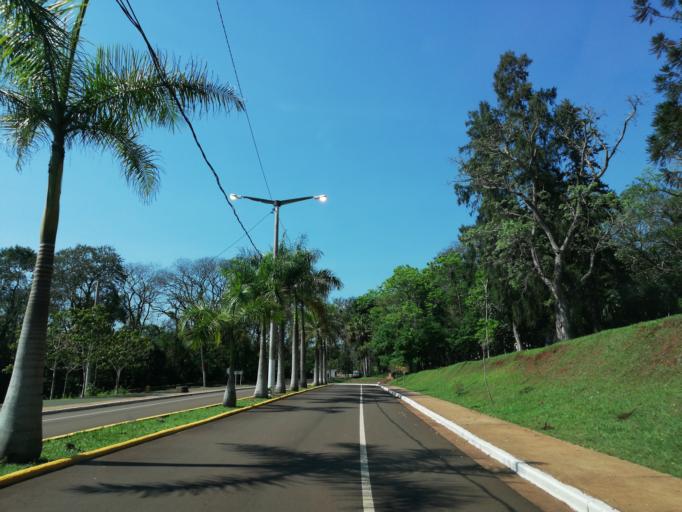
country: AR
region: Misiones
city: Puerto Eldorado
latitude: -26.4091
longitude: -54.6900
